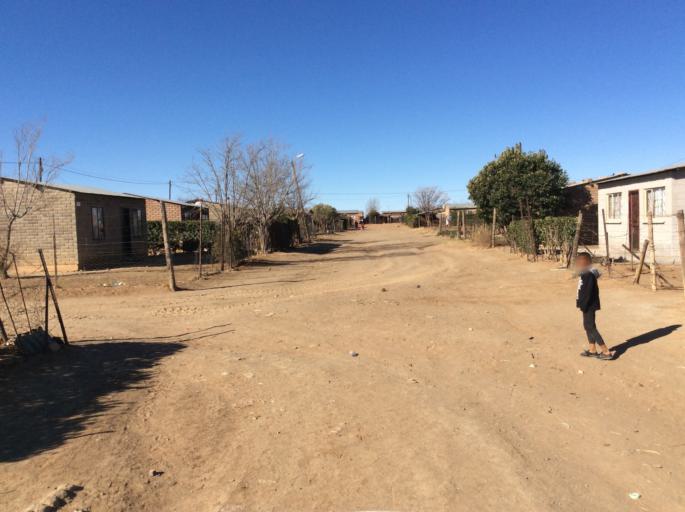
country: ZA
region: Orange Free State
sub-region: Lejweleputswa District Municipality
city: Brandfort
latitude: -28.7323
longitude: 26.1113
